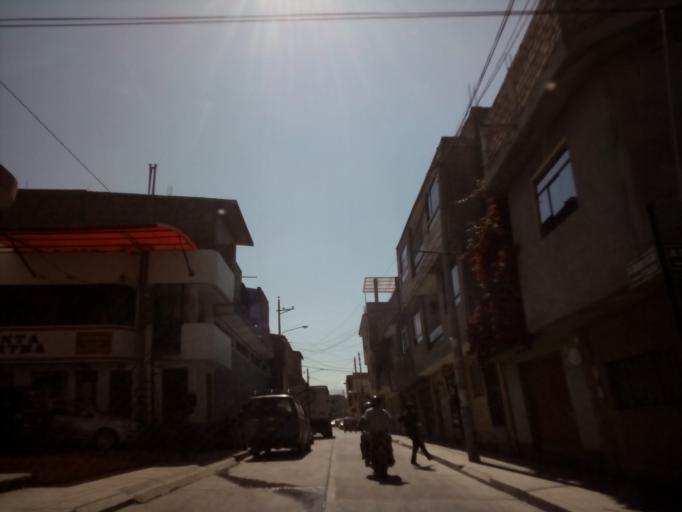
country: PE
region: Ayacucho
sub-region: Provincia de Huamanga
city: Ayacucho
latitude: -13.1567
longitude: -74.2187
